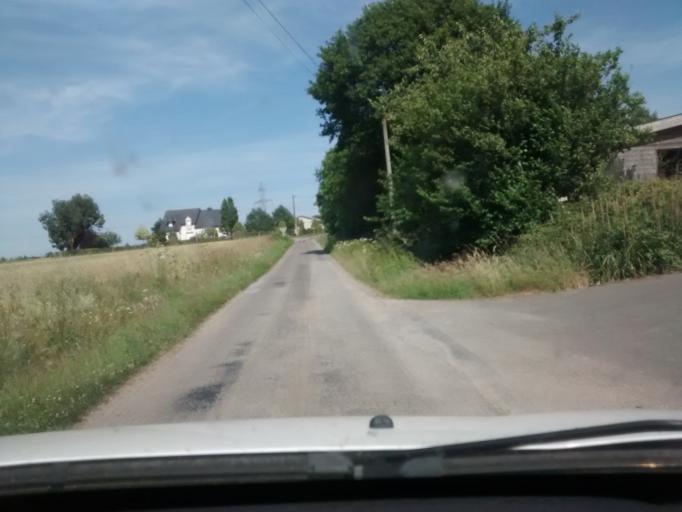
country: FR
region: Brittany
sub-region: Departement d'Ille-et-Vilaine
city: Acigne
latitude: 48.1024
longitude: -1.5654
